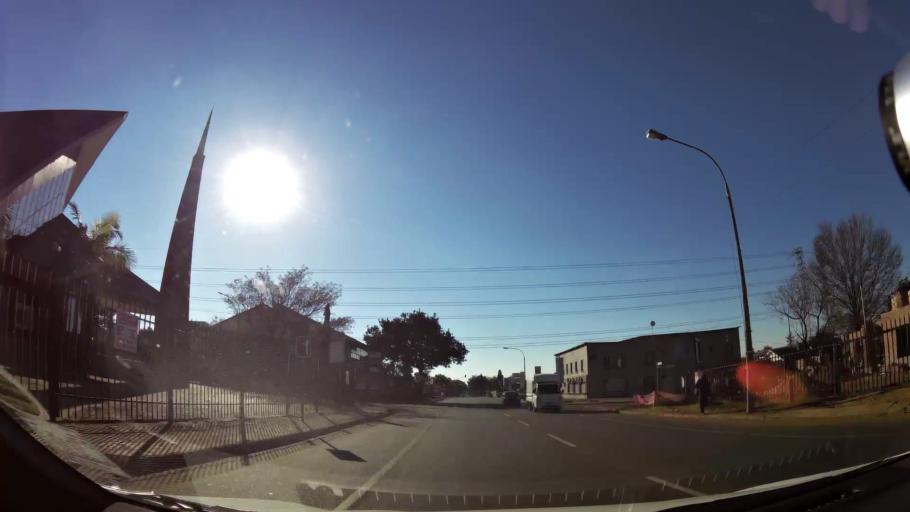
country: ZA
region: Gauteng
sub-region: Ekurhuleni Metropolitan Municipality
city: Germiston
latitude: -26.2852
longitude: 28.1106
